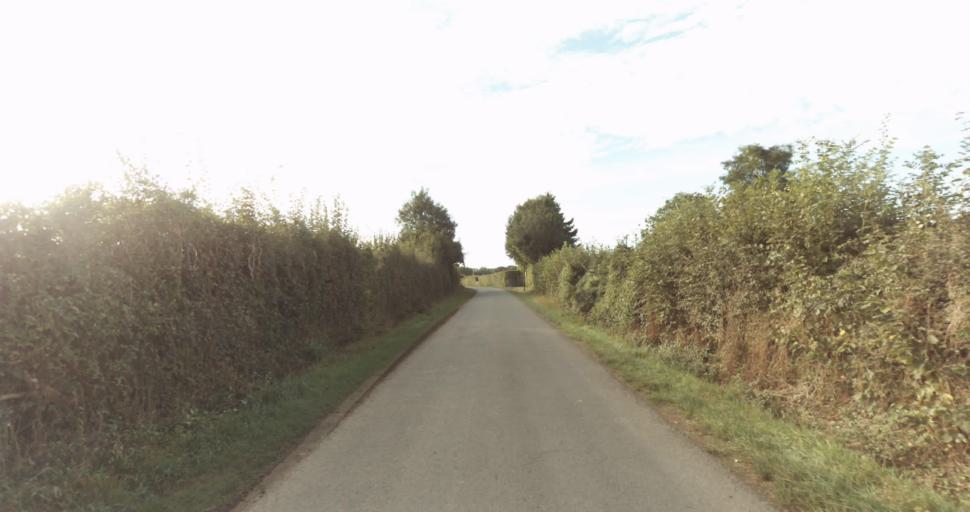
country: FR
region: Lower Normandy
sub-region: Departement de l'Orne
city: Vimoutiers
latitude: 48.8850
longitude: 0.2410
